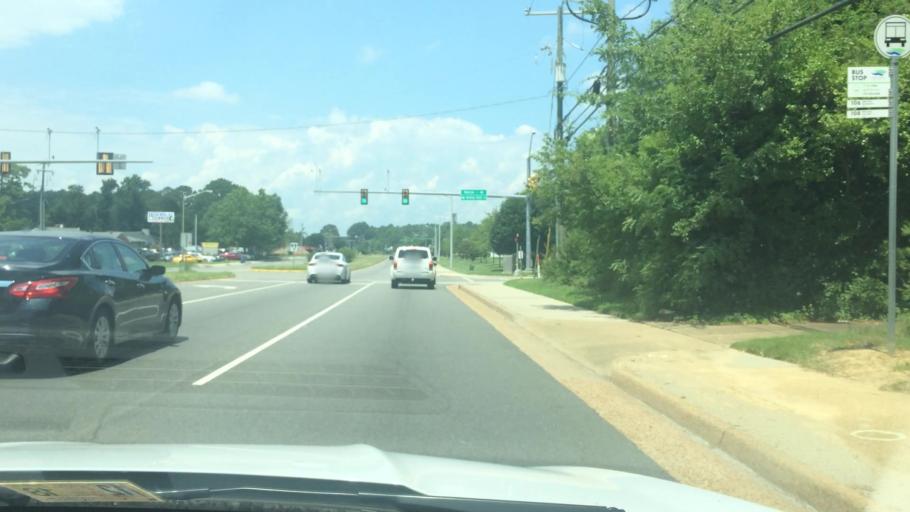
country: US
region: Virginia
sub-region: York County
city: Yorktown
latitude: 37.1409
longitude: -76.5468
